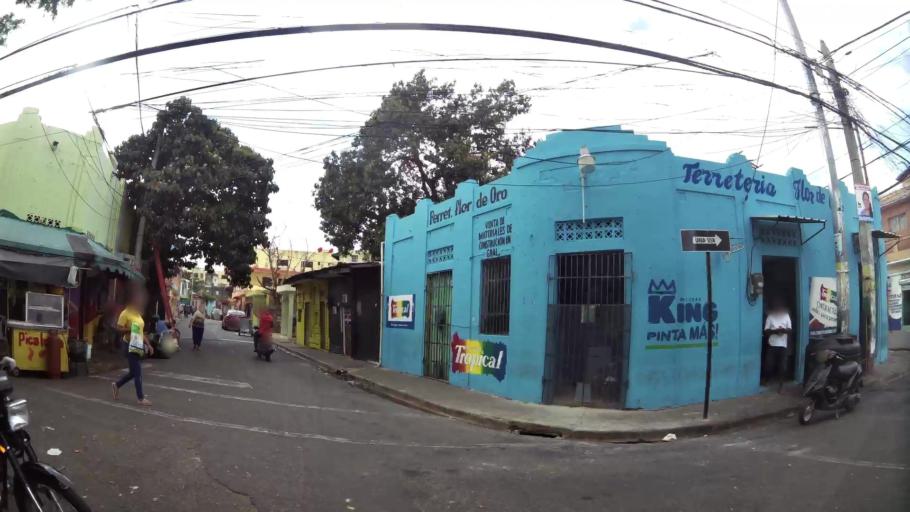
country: DO
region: Nacional
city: San Carlos
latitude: 18.4788
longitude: -69.8945
